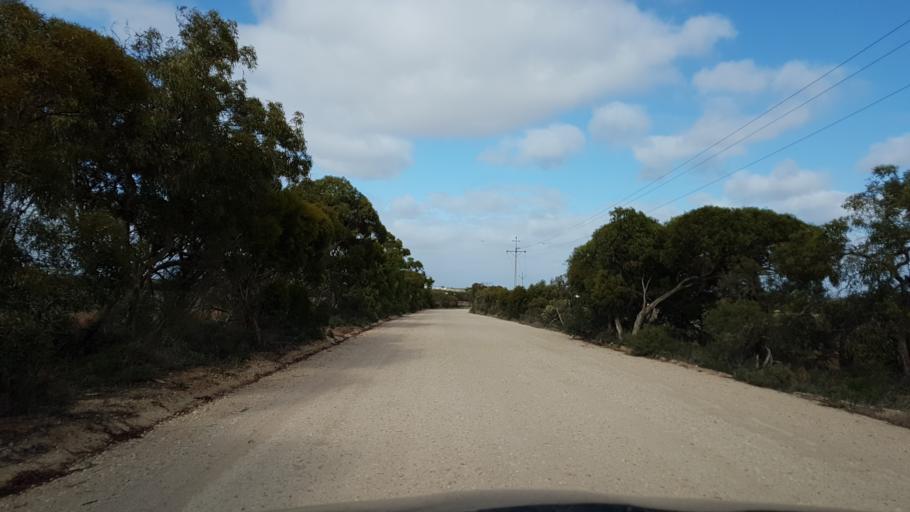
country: AU
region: South Australia
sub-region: Murray Bridge
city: Murray Bridge
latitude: -35.1213
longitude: 139.1872
